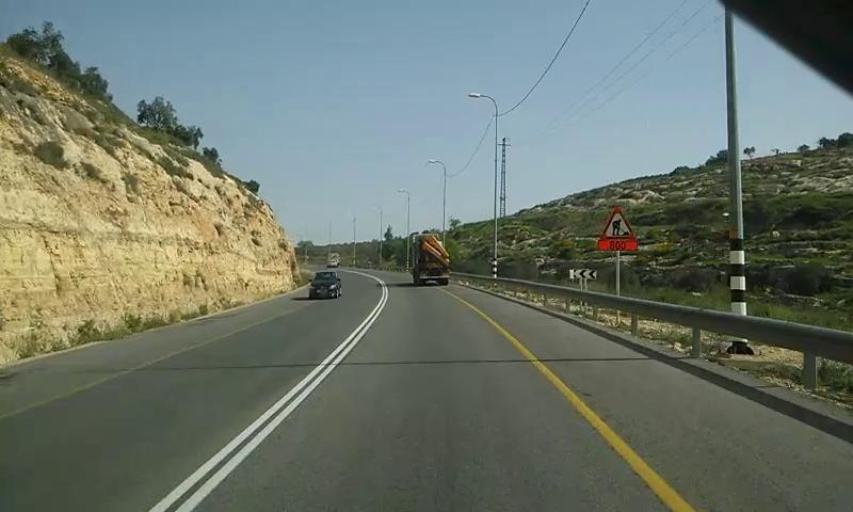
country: PS
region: West Bank
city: Yatma
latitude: 32.1119
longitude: 35.2573
